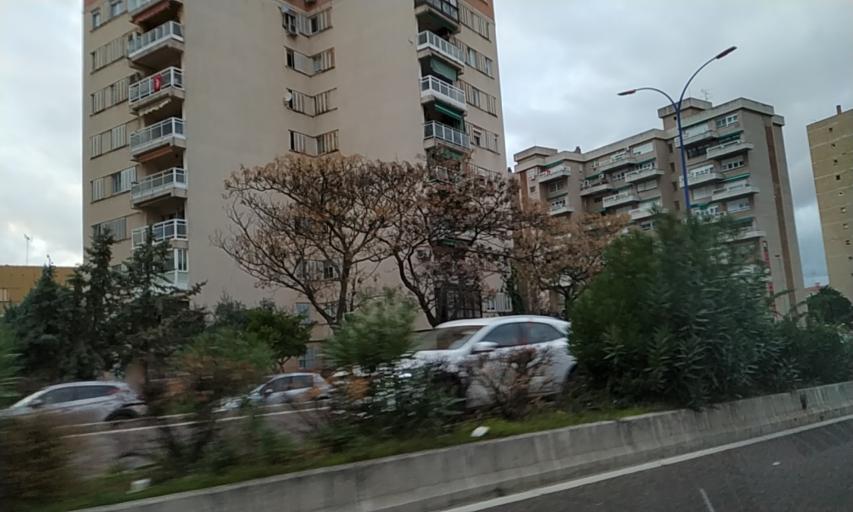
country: ES
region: Extremadura
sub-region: Provincia de Badajoz
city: Badajoz
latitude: 38.8749
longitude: -6.9813
